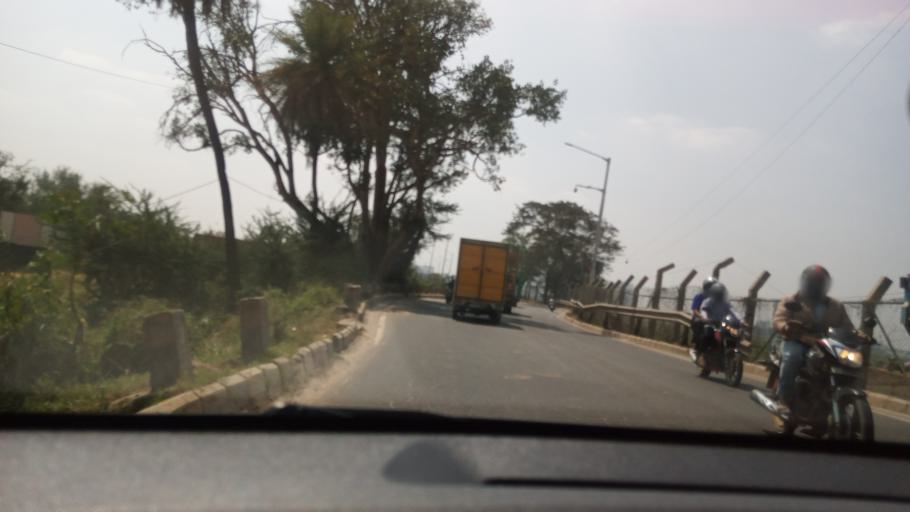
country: IN
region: Karnataka
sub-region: Bangalore Rural
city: Hoskote
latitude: 12.9553
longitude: 77.7443
